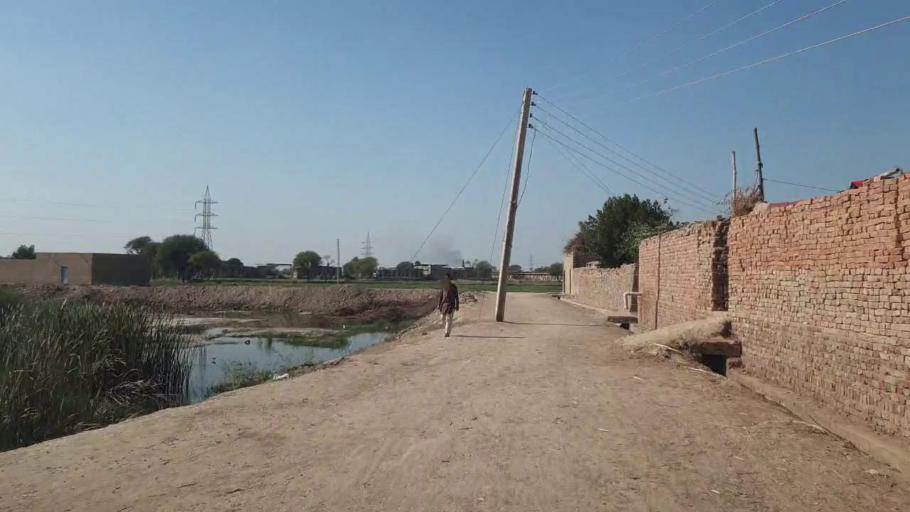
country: PK
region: Sindh
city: Tando Allahyar
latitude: 25.4295
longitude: 68.6926
